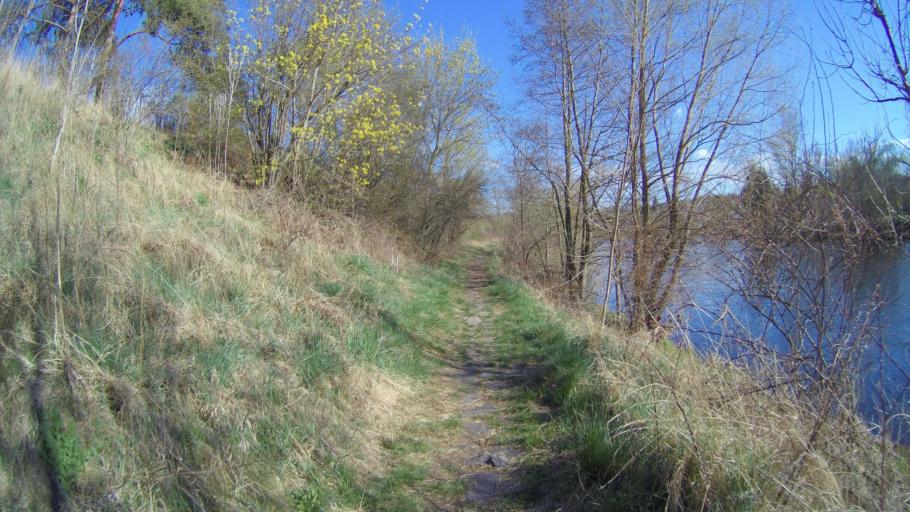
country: CZ
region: Ustecky
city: Zatec
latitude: 50.3298
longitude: 13.5238
